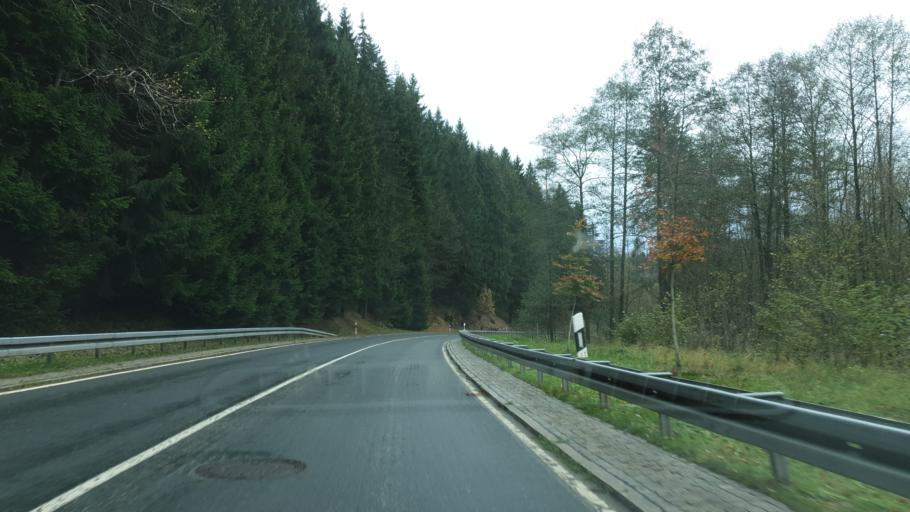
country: DE
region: Saxony
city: Schoenheide
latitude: 50.4971
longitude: 12.5503
